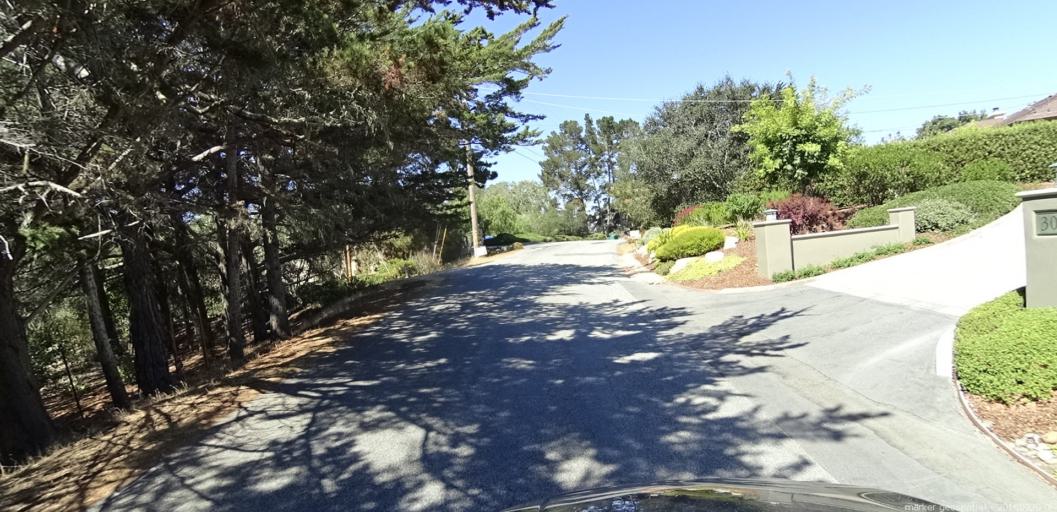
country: US
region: California
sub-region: Monterey County
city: Monterey
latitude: 36.5824
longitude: -121.8721
